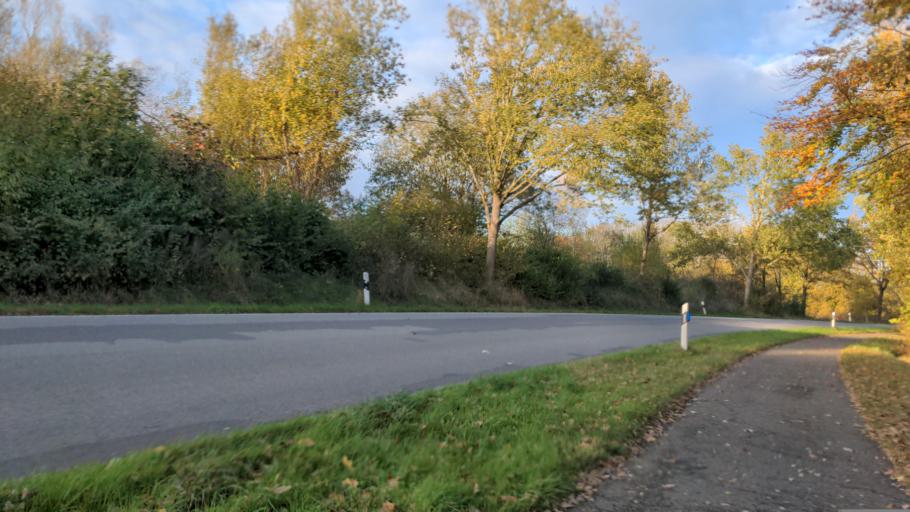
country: DE
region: Schleswig-Holstein
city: Heidekamp
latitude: 53.8604
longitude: 10.5015
